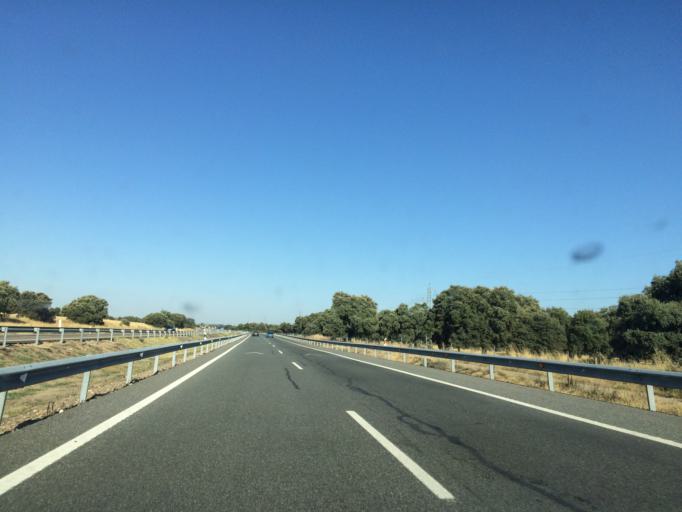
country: ES
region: Castille-La Mancha
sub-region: Province of Toledo
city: Alcanizo
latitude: 39.9231
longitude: -5.0898
